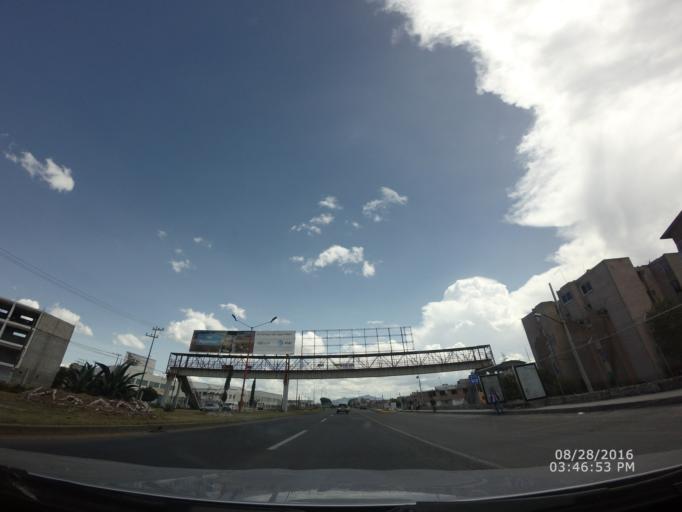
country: MX
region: Hidalgo
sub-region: Mineral de la Reforma
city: Nuevo Centro de Poblacion Agricola el Chacon
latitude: 20.0712
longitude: -98.7447
